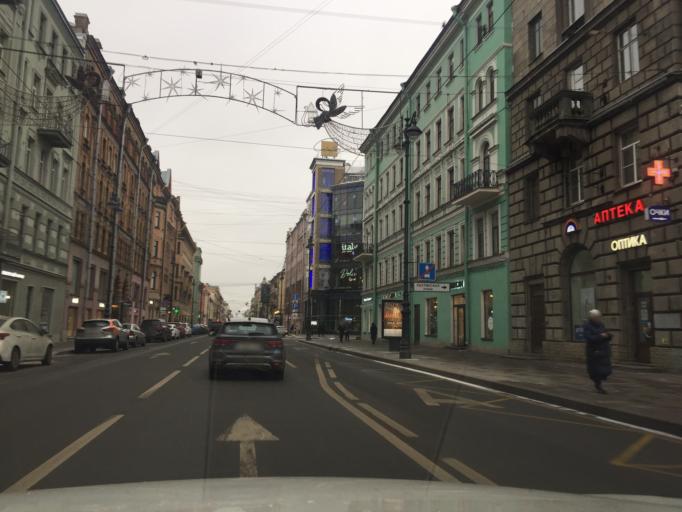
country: RU
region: St.-Petersburg
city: Petrogradka
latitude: 59.9616
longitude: 30.3052
